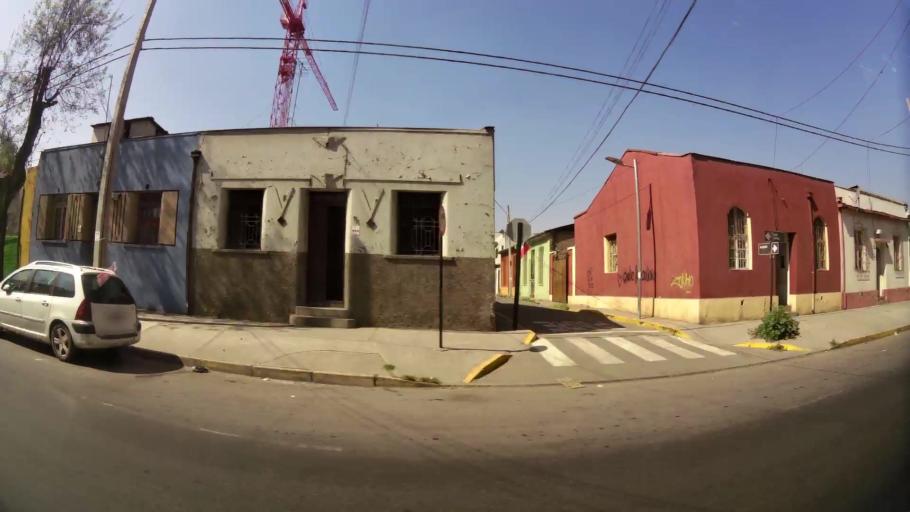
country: CL
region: Santiago Metropolitan
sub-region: Provincia de Santiago
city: Lo Prado
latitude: -33.4515
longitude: -70.6899
